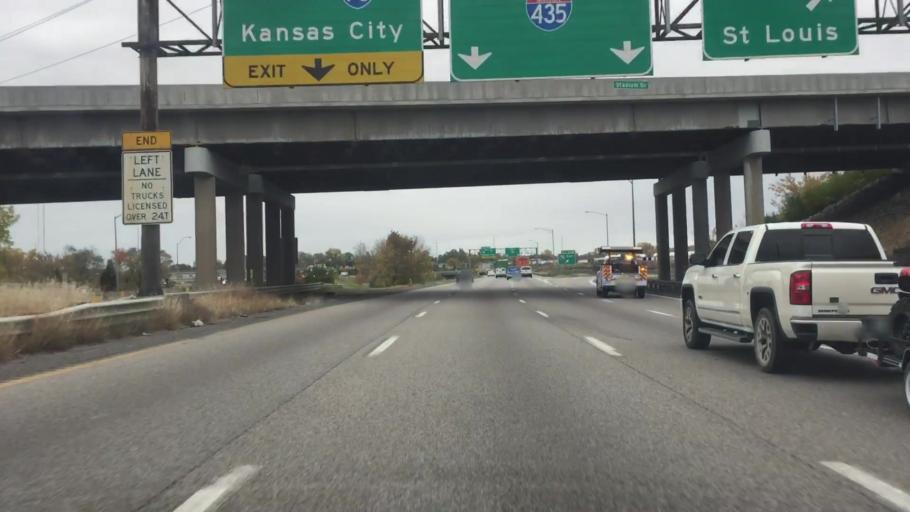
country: US
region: Missouri
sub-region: Jackson County
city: Raytown
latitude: 39.0555
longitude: -94.4940
